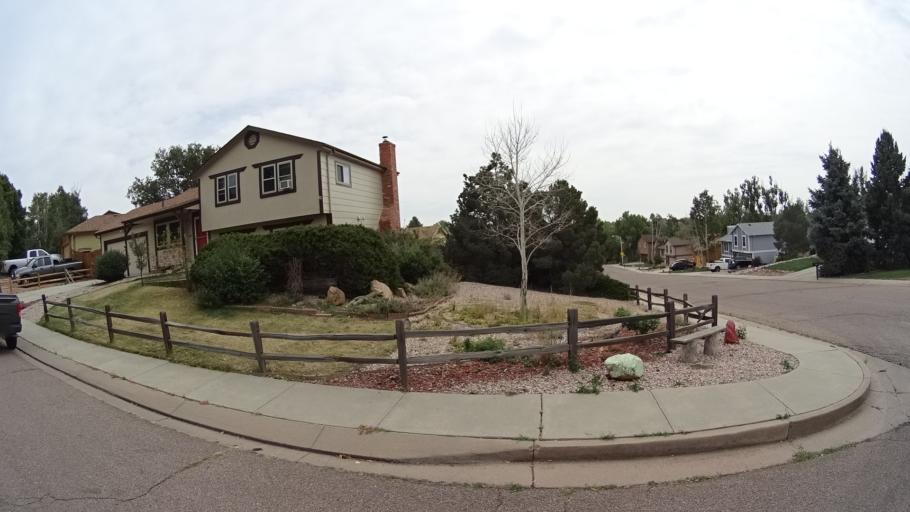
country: US
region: Colorado
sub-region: El Paso County
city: Cimarron Hills
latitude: 38.9050
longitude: -104.7244
